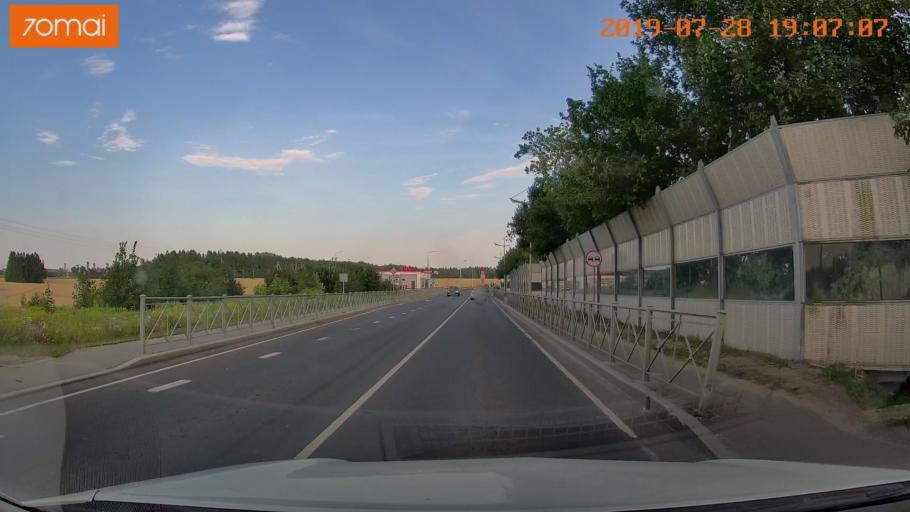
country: RU
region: Kaliningrad
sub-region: Gorod Svetlogorsk
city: Svetlogorsk
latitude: 54.9288
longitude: 20.1695
